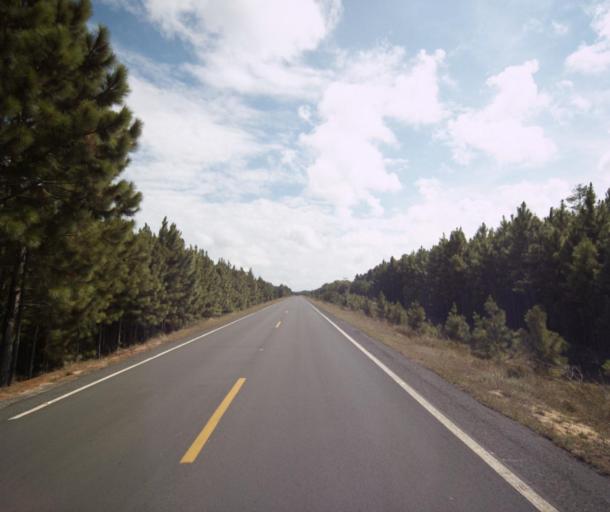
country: BR
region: Rio Grande do Sul
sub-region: Sao Lourenco Do Sul
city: Sao Lourenco do Sul
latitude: -31.4579
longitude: -51.2231
